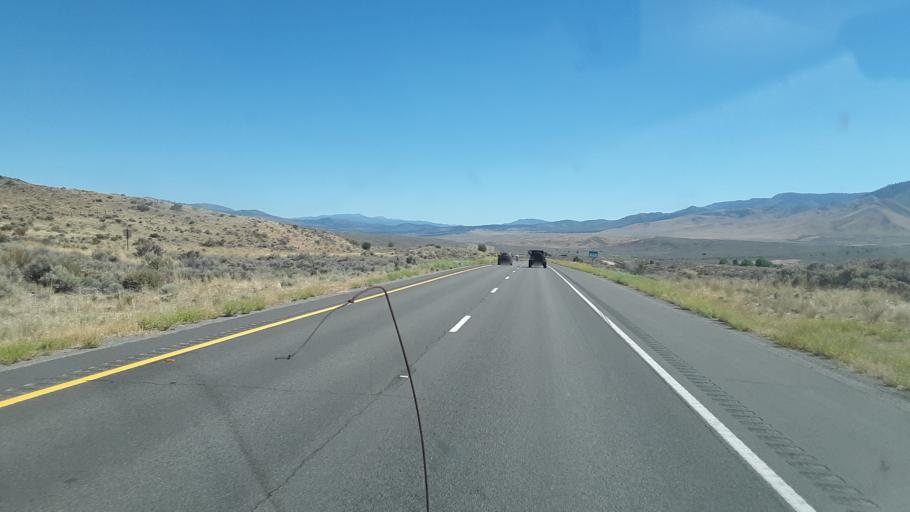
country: US
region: Nevada
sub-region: Washoe County
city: Cold Springs
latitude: 39.7462
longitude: -120.0397
